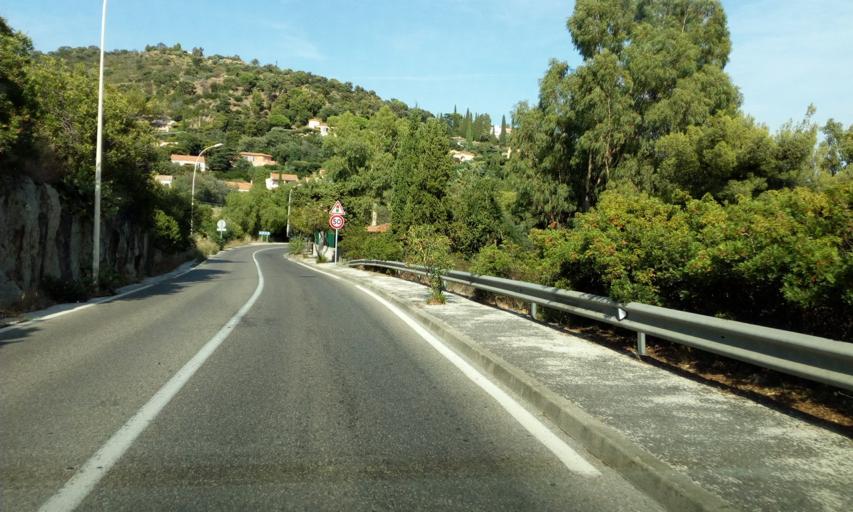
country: FR
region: Provence-Alpes-Cote d'Azur
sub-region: Departement du Var
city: Le Lavandou
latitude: 43.1455
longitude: 6.3931
